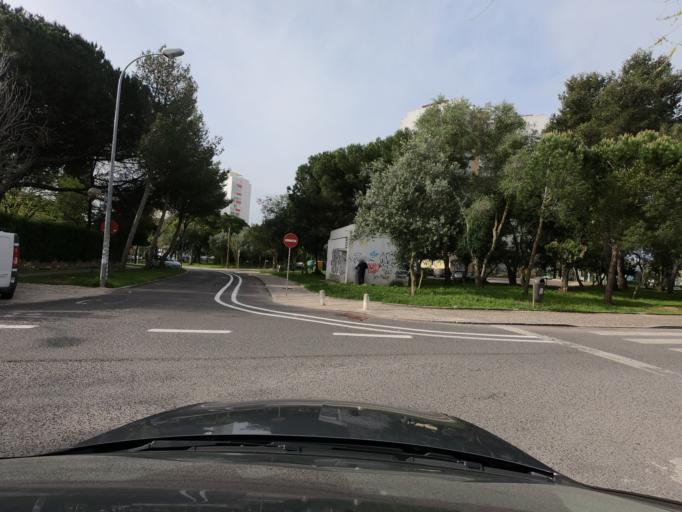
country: PT
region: Lisbon
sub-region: Oeiras
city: Carcavelos
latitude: 38.6935
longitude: -9.3219
